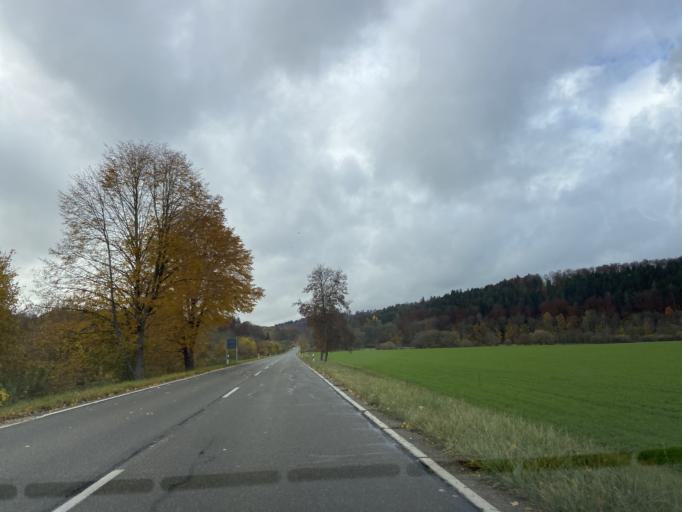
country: DE
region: Baden-Wuerttemberg
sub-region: Tuebingen Region
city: Inzigkofen
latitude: 48.0792
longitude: 9.1870
